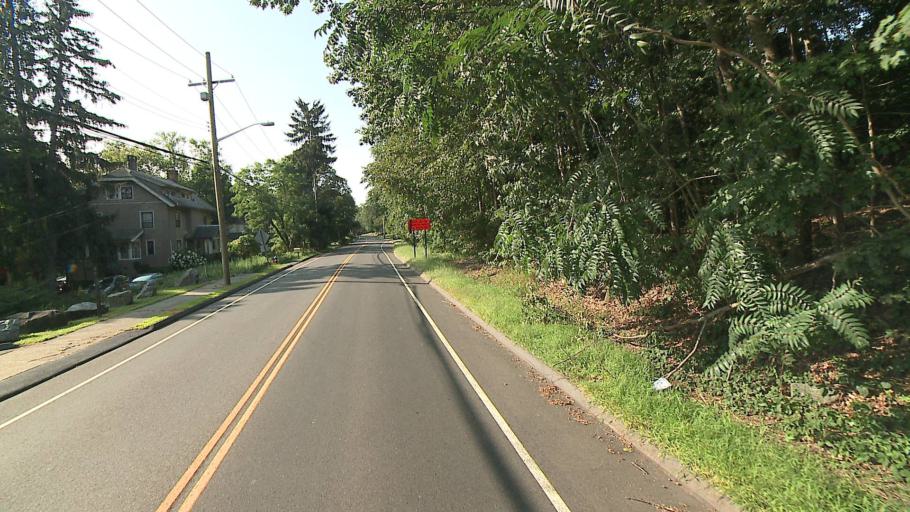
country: US
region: Connecticut
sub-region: New Haven County
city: New Haven
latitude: 41.3114
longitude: -72.9702
